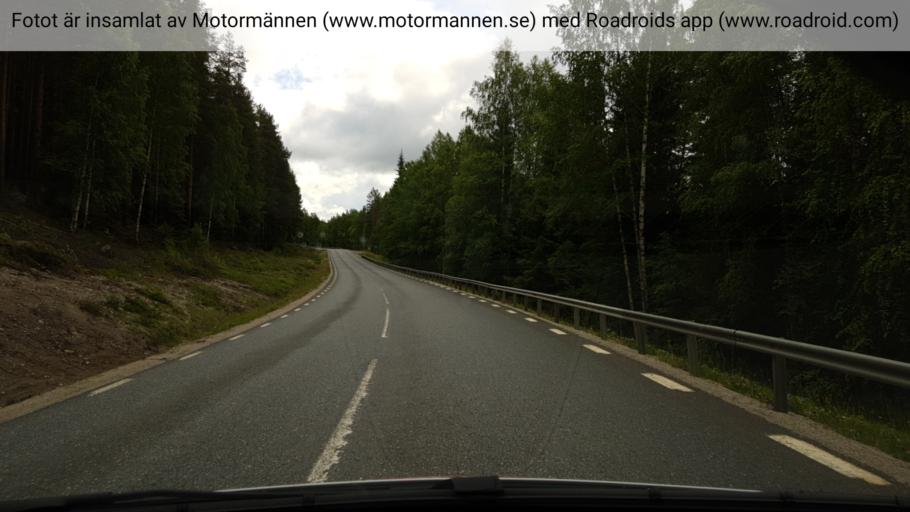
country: SE
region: Vaesterbotten
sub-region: Lycksele Kommun
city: Lycksele
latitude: 64.4200
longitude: 19.0041
